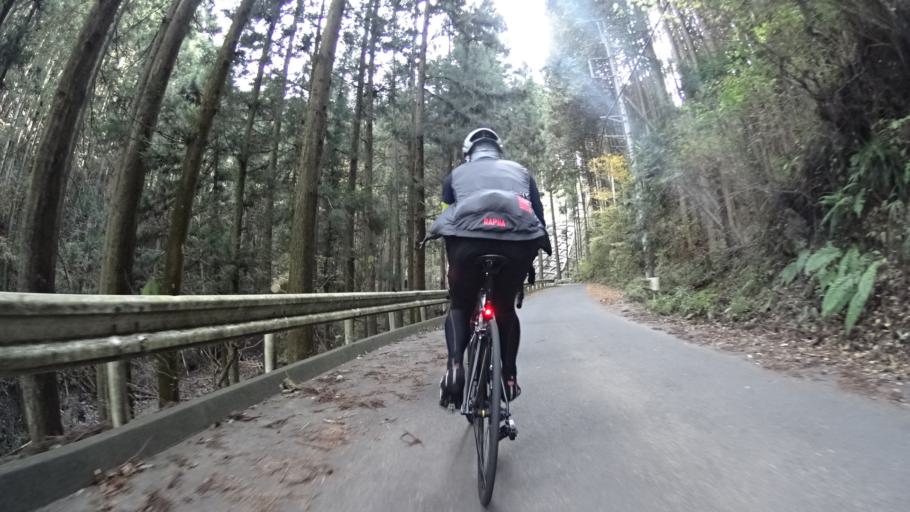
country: JP
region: Saitama
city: Chichibu
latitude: 35.9154
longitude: 139.1774
